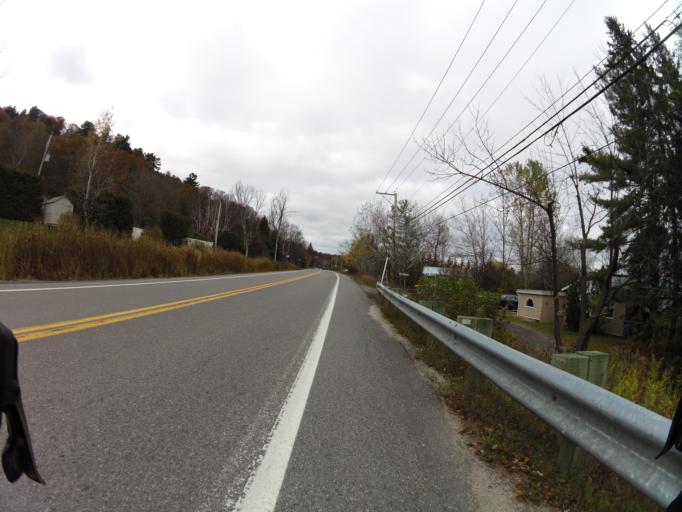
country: CA
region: Quebec
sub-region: Outaouais
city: Wakefield
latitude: 45.5408
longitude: -75.8157
